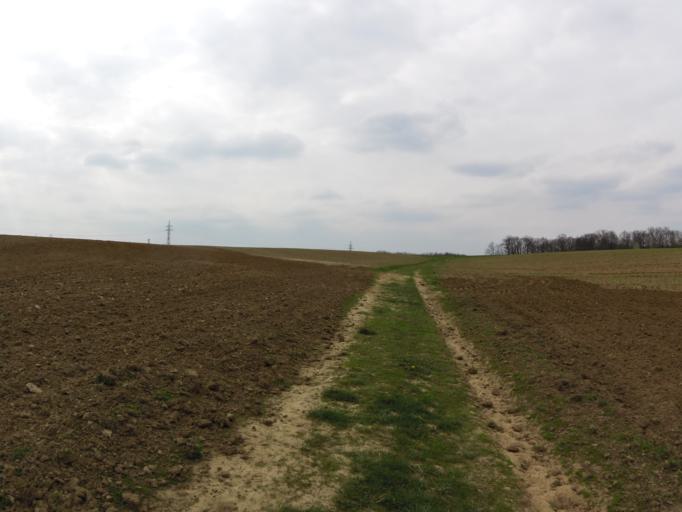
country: DE
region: Bavaria
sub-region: Regierungsbezirk Unterfranken
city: Rottendorf
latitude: 49.7943
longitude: 10.0187
